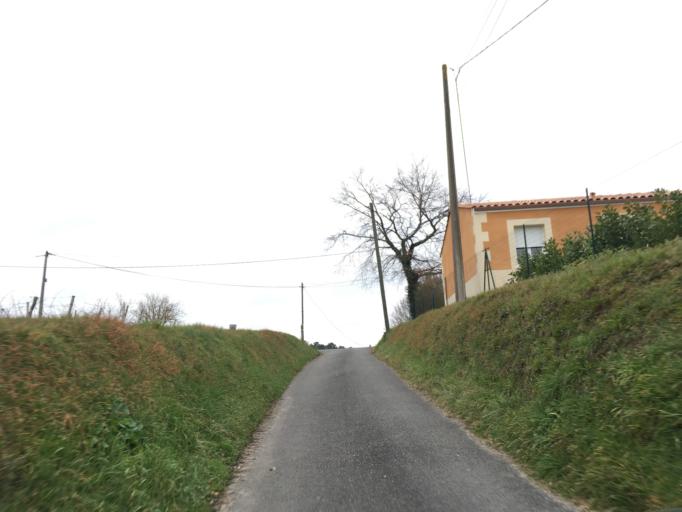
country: FR
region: Aquitaine
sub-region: Departement de la Gironde
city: Saint-Ciers-sur-Gironde
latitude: 45.3072
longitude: -0.5853
